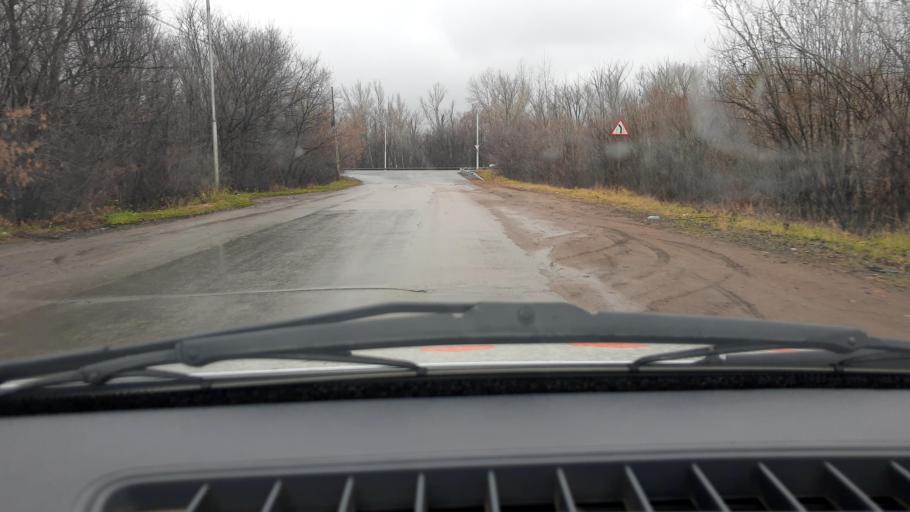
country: RU
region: Bashkortostan
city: Iglino
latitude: 54.7958
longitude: 56.2098
